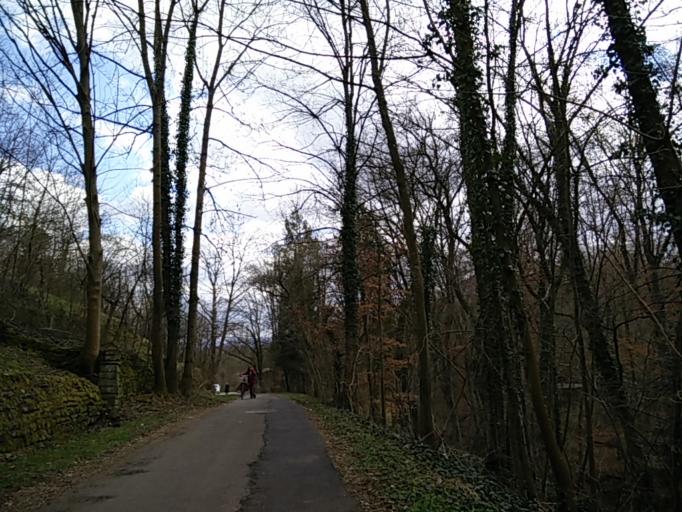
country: DE
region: Baden-Wuerttemberg
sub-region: Tuebingen Region
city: Tuebingen
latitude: 48.5352
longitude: 9.0415
